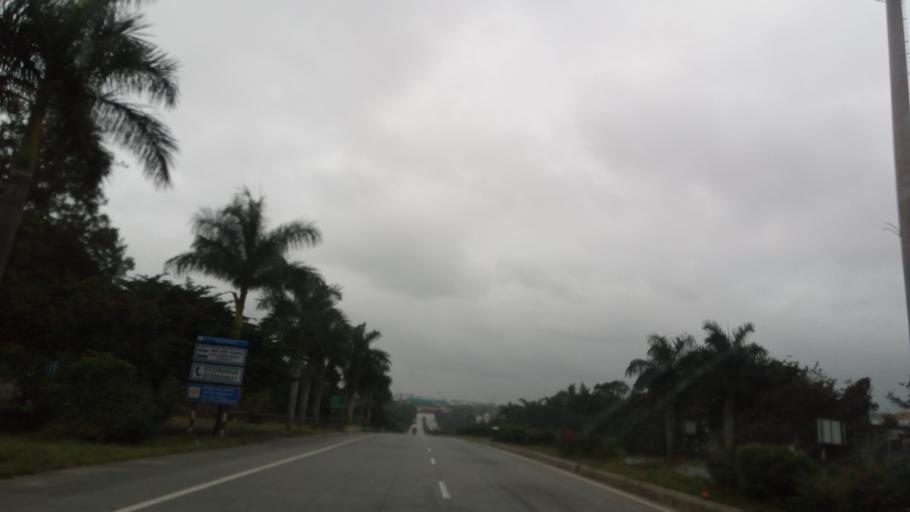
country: IN
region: Karnataka
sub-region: Bangalore Urban
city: Bangalore
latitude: 12.9273
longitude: 77.5317
